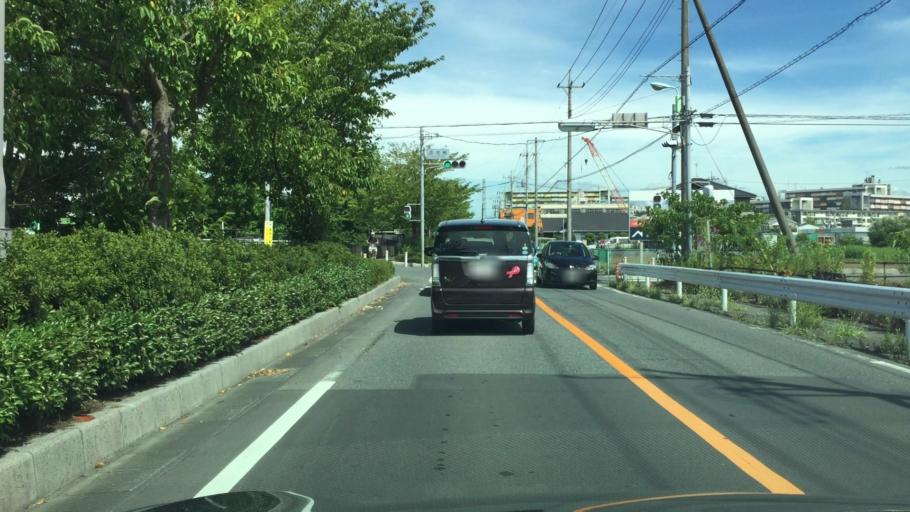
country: JP
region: Saitama
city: Yashio-shi
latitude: 35.8526
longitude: 139.8534
